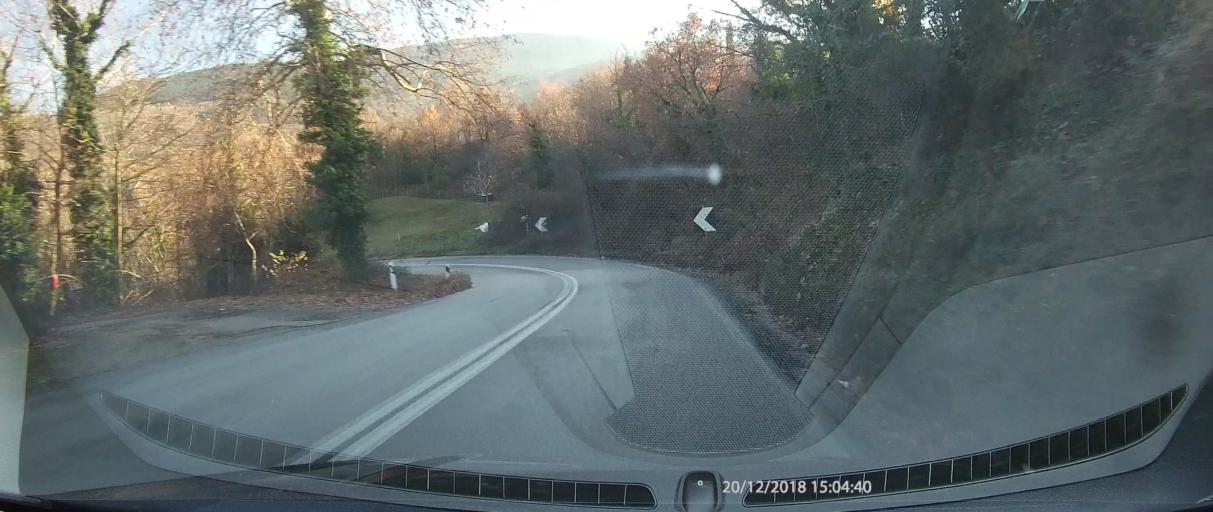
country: GR
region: Central Greece
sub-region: Nomos Evrytanias
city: Karpenisi
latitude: 38.9115
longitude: 21.9265
